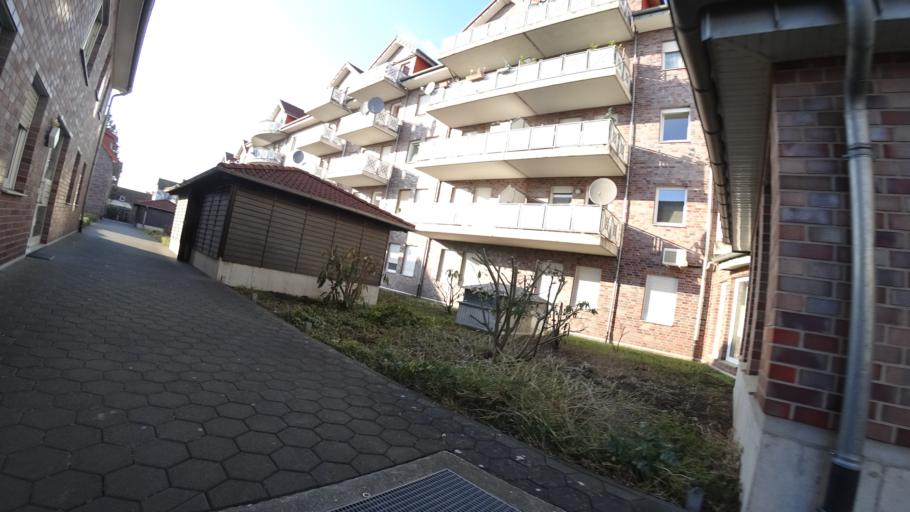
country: DE
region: North Rhine-Westphalia
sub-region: Regierungsbezirk Detmold
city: Guetersloh
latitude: 51.9048
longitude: 8.3903
